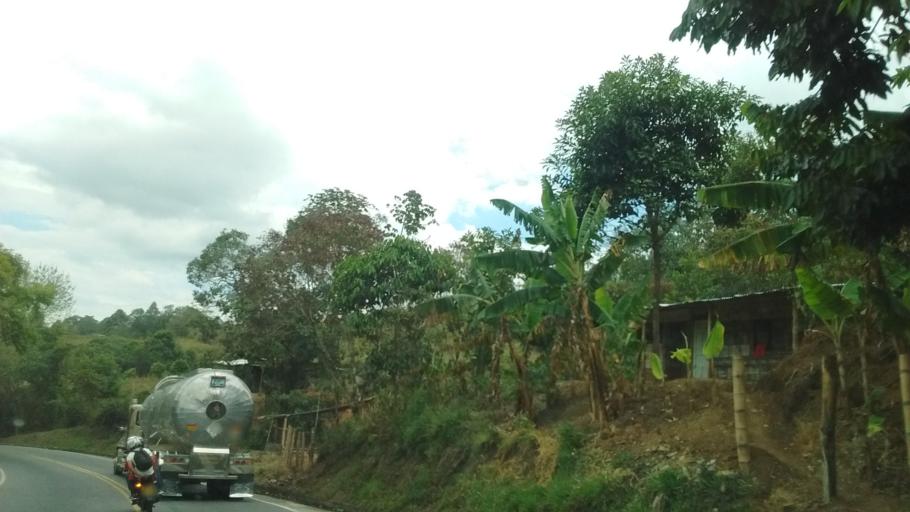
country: CO
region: Cauca
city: Rosas
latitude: 2.3096
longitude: -76.6881
